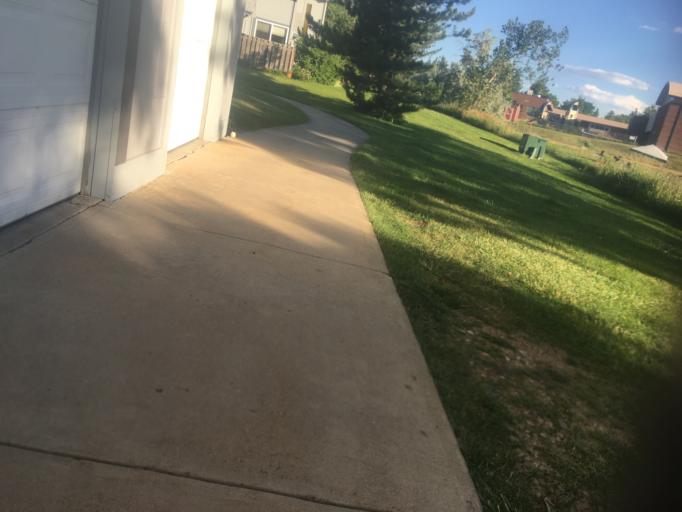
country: US
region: Colorado
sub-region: Boulder County
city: Boulder
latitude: 40.0056
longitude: -105.2431
